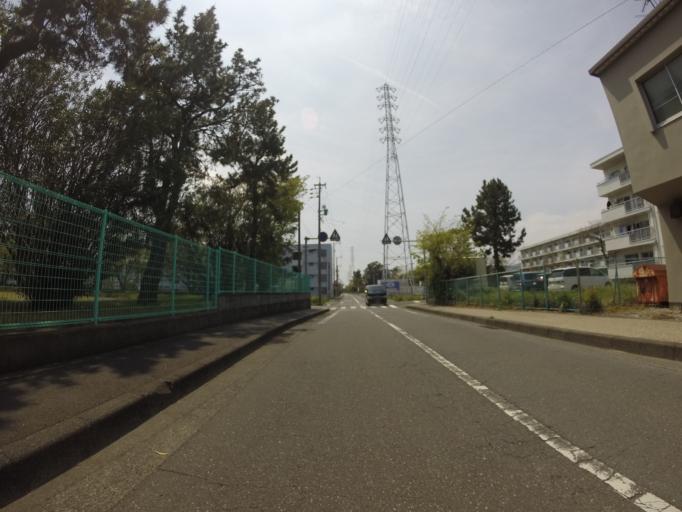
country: JP
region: Shizuoka
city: Shizuoka-shi
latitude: 34.9863
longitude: 138.5117
